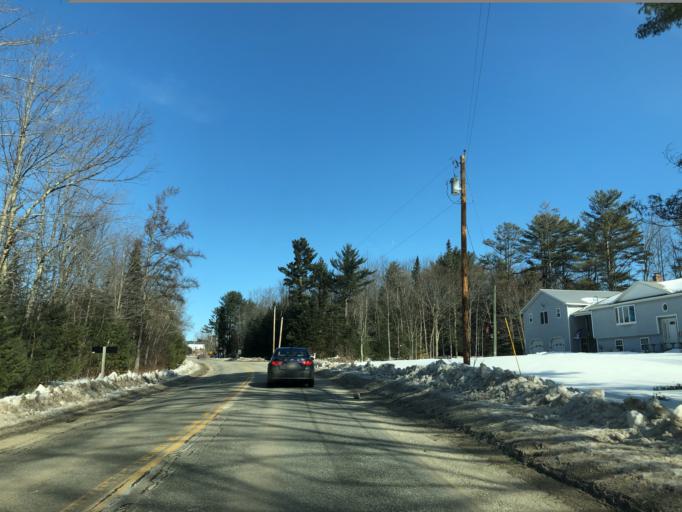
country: US
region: Maine
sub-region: Oxford County
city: Buckfield
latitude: 44.2315
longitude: -70.3370
